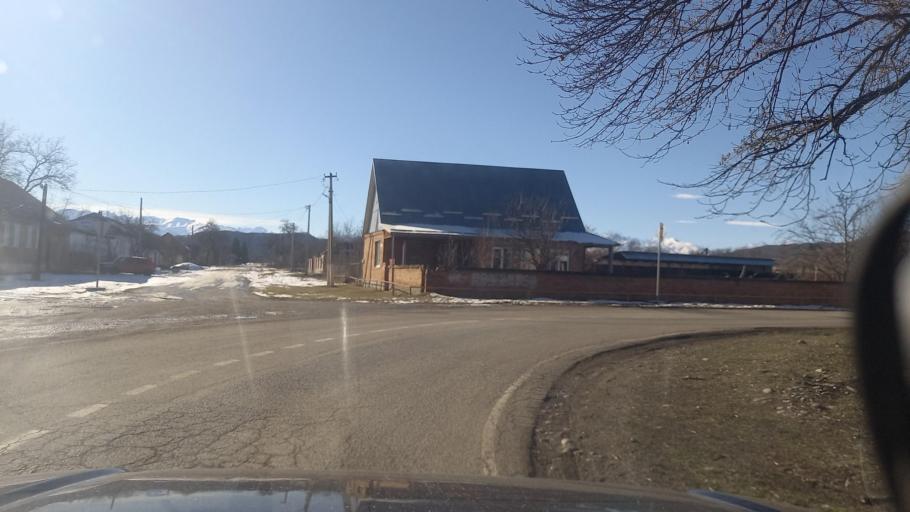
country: RU
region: Kabardino-Balkariya
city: Urukh
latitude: 43.2653
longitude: 43.9920
